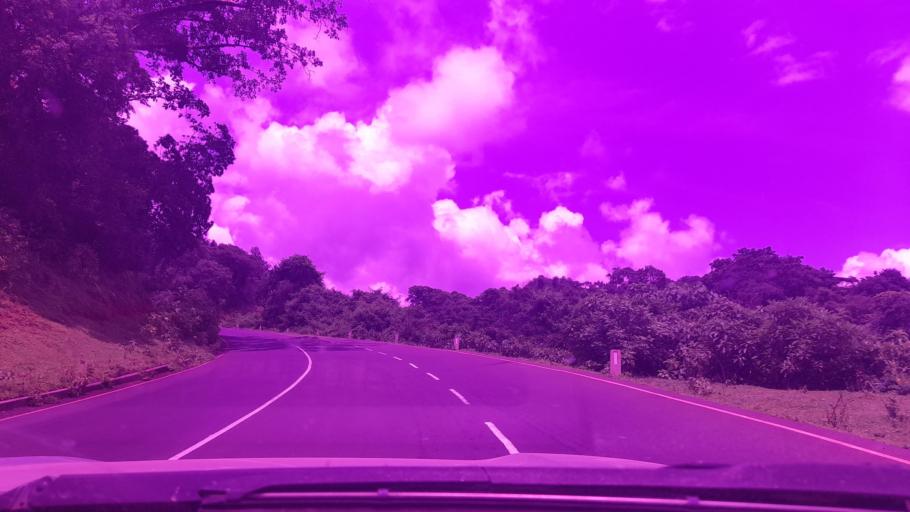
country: ET
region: Oromiya
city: Metu
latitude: 8.3400
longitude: 35.7406
